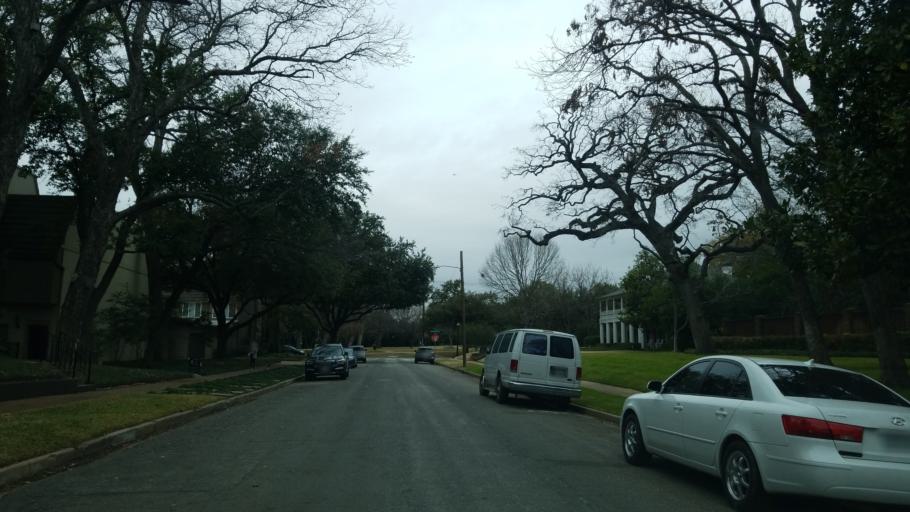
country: US
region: Texas
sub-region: Dallas County
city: Highland Park
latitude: 32.8183
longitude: -96.8150
